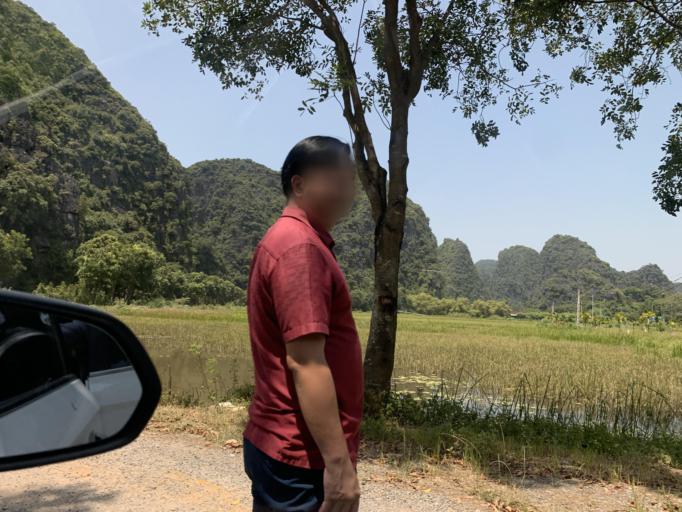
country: VN
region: Ninh Binh
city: Thanh Pho Ninh Binh
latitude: 20.2221
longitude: 105.9313
